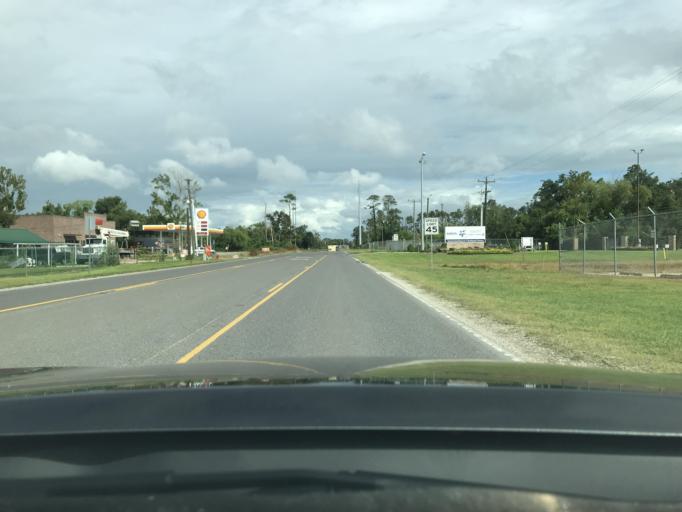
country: US
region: Louisiana
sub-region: Calcasieu Parish
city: Westlake
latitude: 30.2524
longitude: -93.2729
